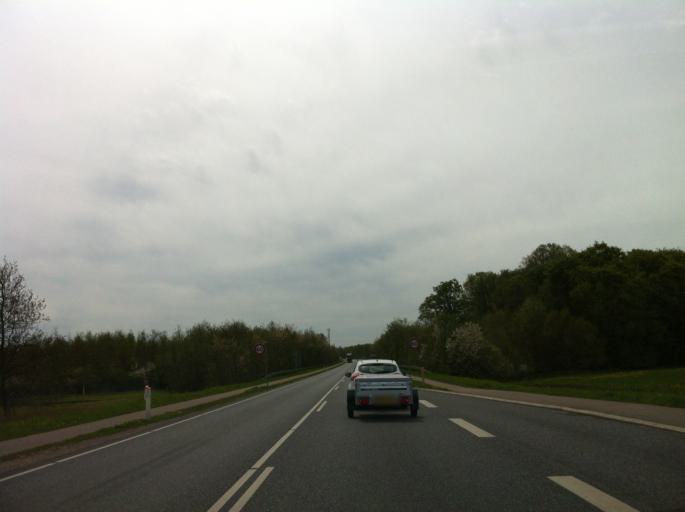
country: DK
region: Zealand
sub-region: Ringsted Kommune
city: Ringsted
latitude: 55.4627
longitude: 11.8264
